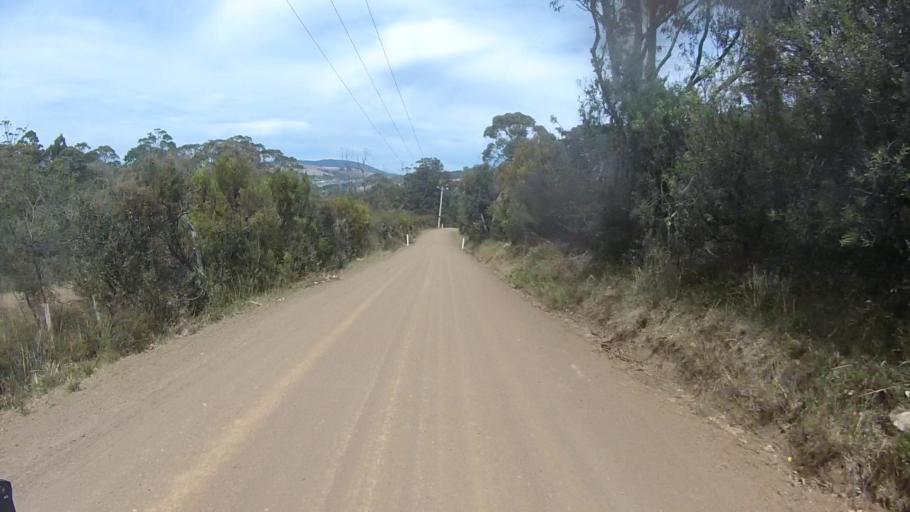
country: AU
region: Tasmania
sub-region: Sorell
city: Sorell
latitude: -42.7921
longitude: 147.8459
